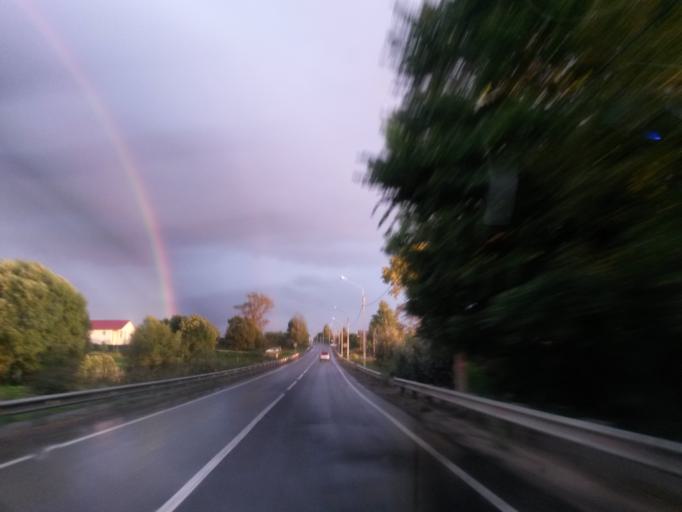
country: RU
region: Jaroslavl
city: Gavrilov-Yam
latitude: 57.3516
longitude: 39.9085
